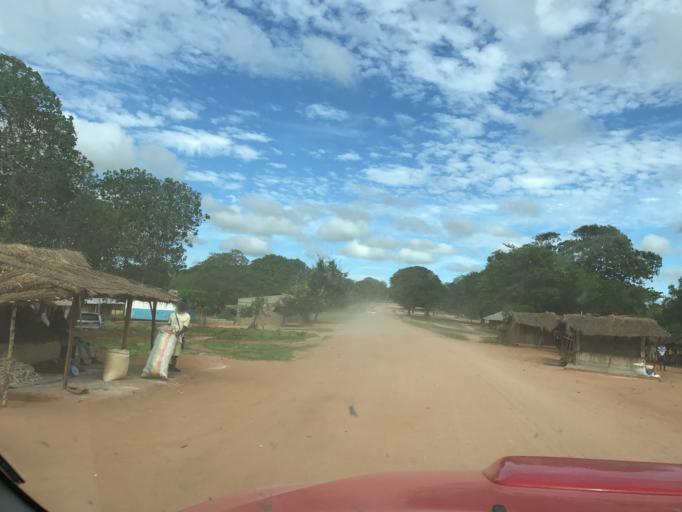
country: MZ
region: Nampula
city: Nacala
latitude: -14.4976
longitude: 40.5627
